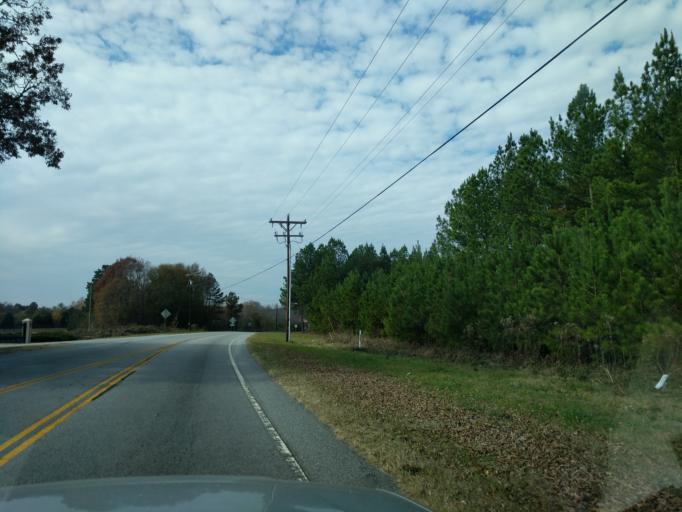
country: US
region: South Carolina
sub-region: Anderson County
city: Piedmont
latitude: 34.7102
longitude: -82.5042
